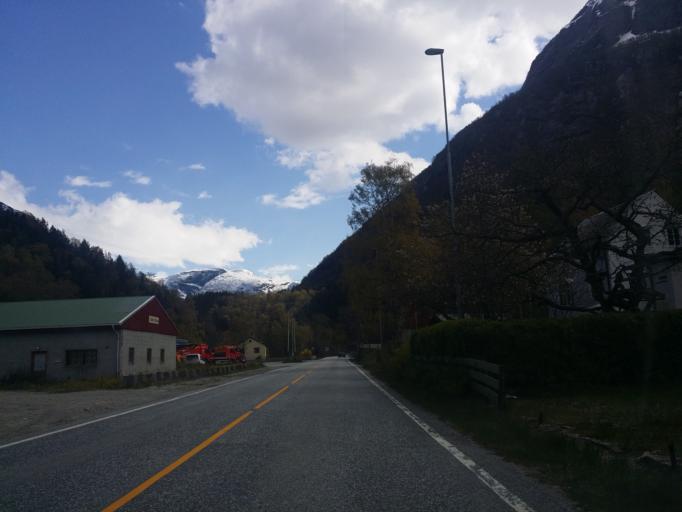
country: NO
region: Hordaland
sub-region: Eidfjord
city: Eidfjord
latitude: 60.4614
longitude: 7.0795
